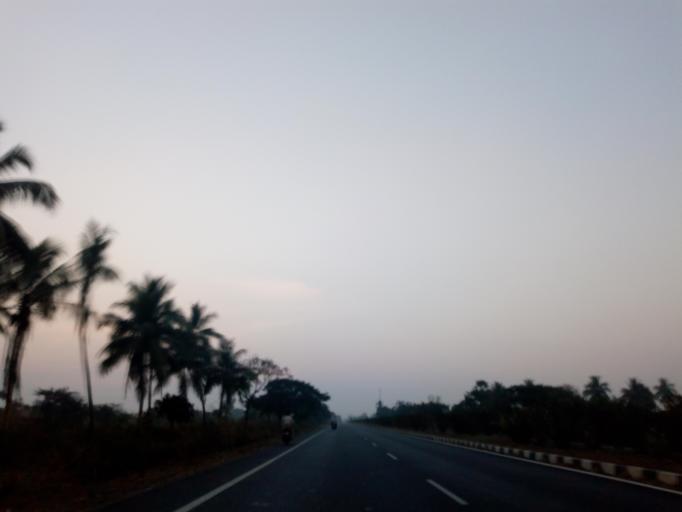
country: IN
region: Andhra Pradesh
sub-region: West Godavari
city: Tadepallegudem
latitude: 16.8240
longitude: 81.4428
